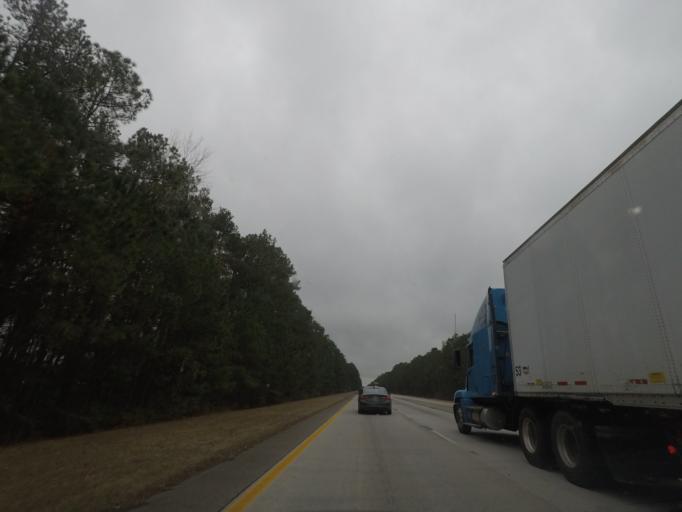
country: US
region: South Carolina
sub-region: Colleton County
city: Walterboro
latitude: 32.9992
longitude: -80.6704
